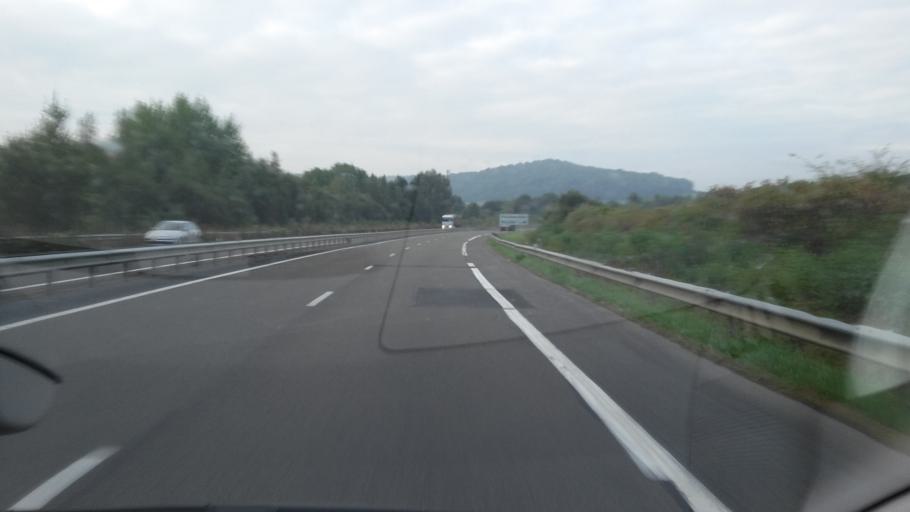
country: FR
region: Champagne-Ardenne
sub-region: Departement des Ardennes
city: La Francheville
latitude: 49.7020
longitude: 4.6961
